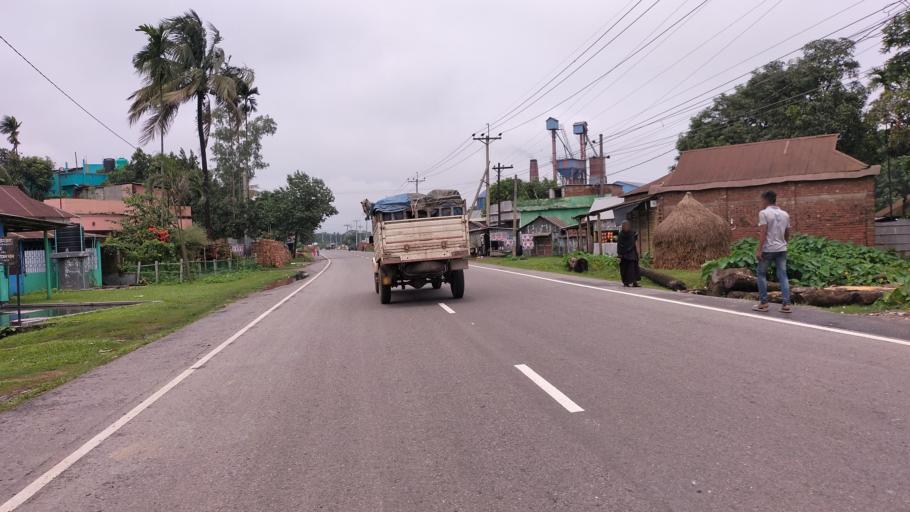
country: BD
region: Dhaka
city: Netrakona
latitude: 24.8499
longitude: 90.6457
